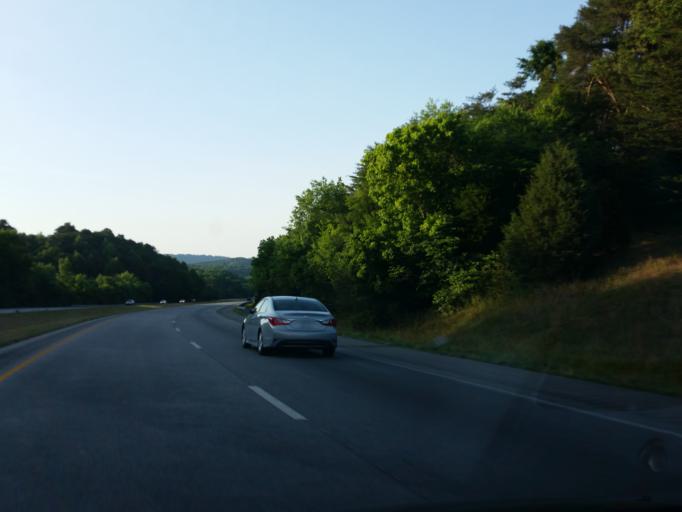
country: US
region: Georgia
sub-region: Dade County
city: Trenton
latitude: 34.7993
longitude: -85.5499
